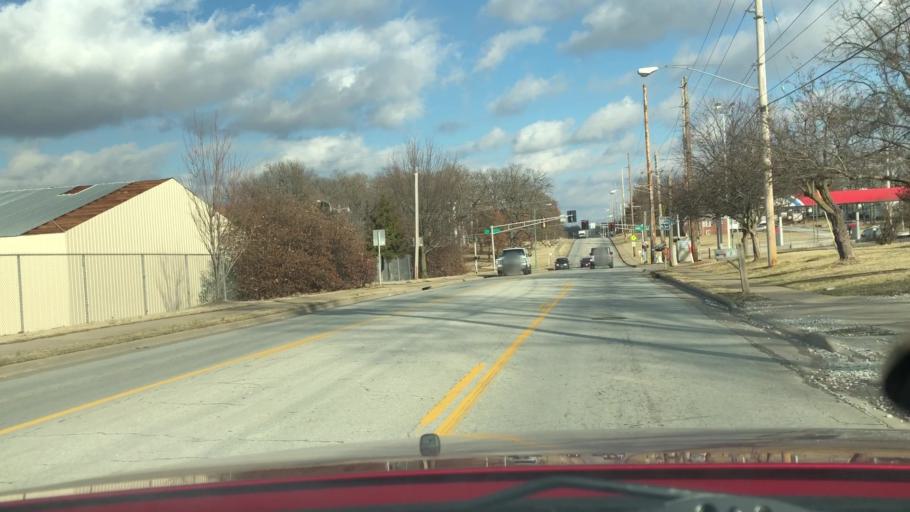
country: US
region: Missouri
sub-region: Greene County
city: Springfield
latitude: 37.2516
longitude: -93.2983
